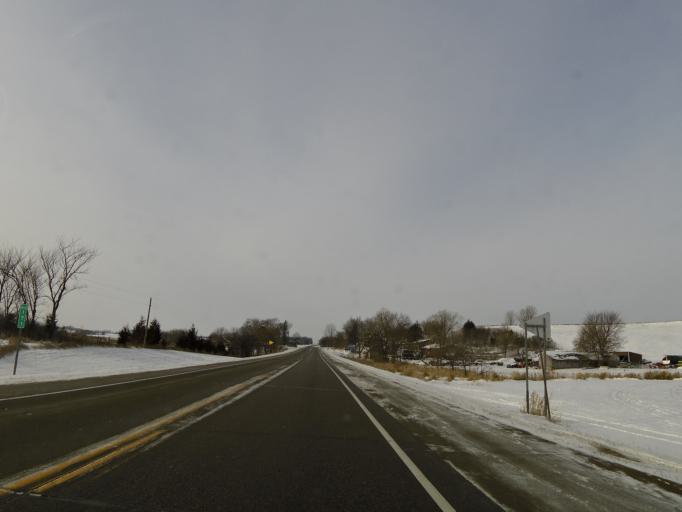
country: US
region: Minnesota
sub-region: Hennepin County
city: Saint Bonifacius
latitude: 44.9054
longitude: -93.7875
